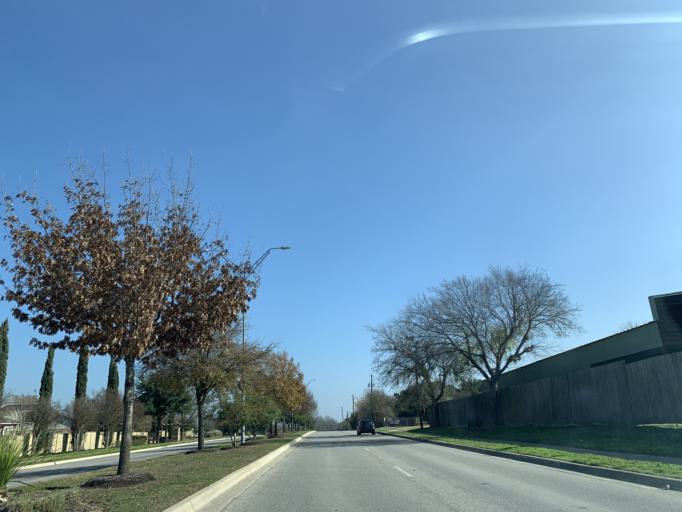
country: US
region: Texas
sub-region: Williamson County
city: Round Rock
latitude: 30.5087
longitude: -97.6329
